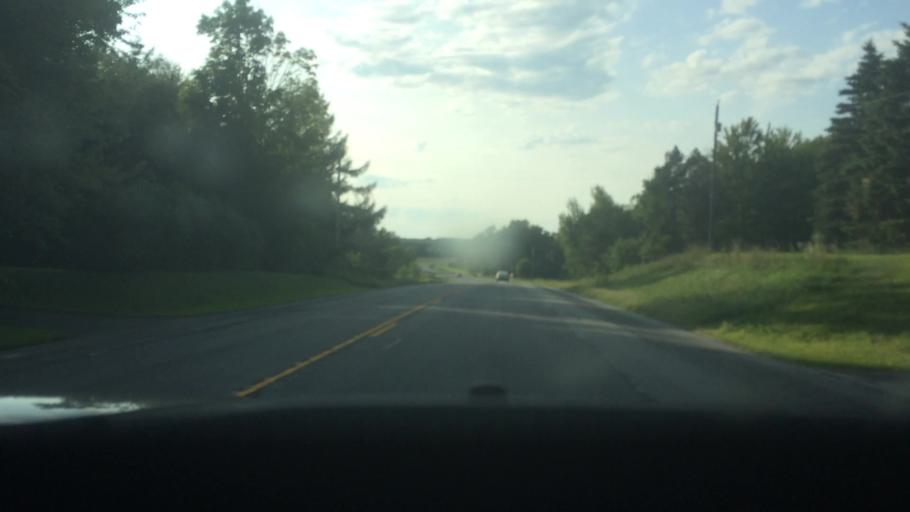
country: US
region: New York
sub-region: St. Lawrence County
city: Canton
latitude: 44.6058
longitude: -75.2060
